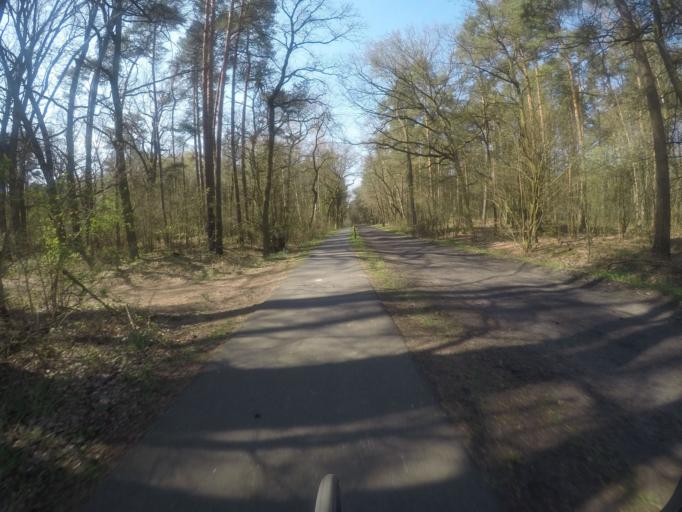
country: DE
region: Brandenburg
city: Brieselang
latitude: 52.6589
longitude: 12.9501
